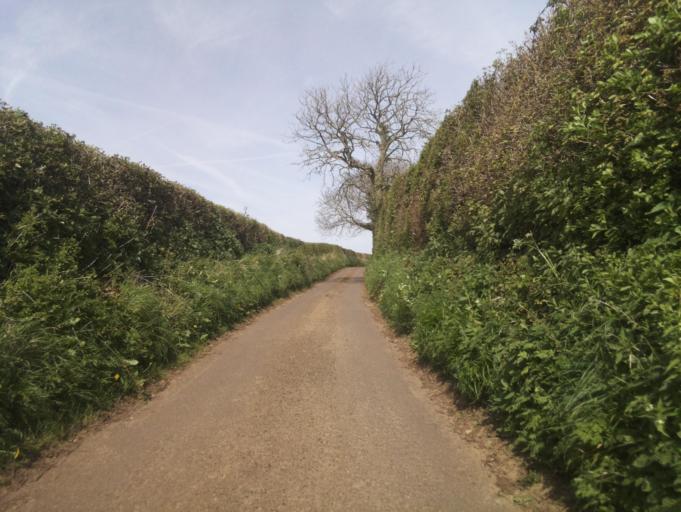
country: GB
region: England
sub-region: Dorset
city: Sherborne
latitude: 50.9631
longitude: -2.5184
